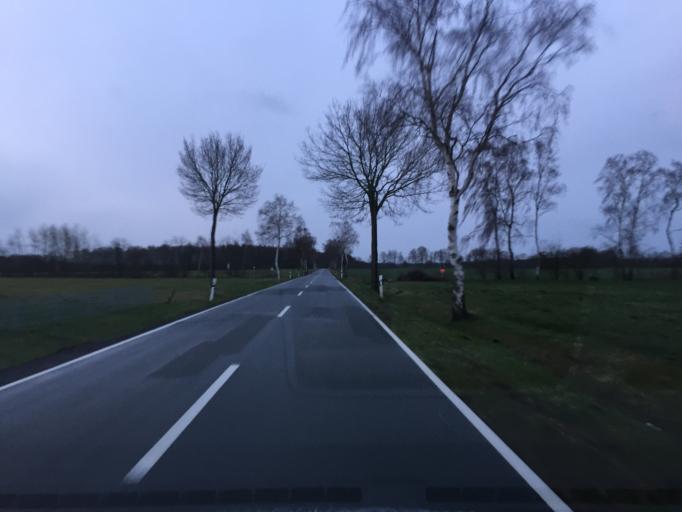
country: DE
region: Lower Saxony
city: Maasen
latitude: 52.6528
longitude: 8.8848
